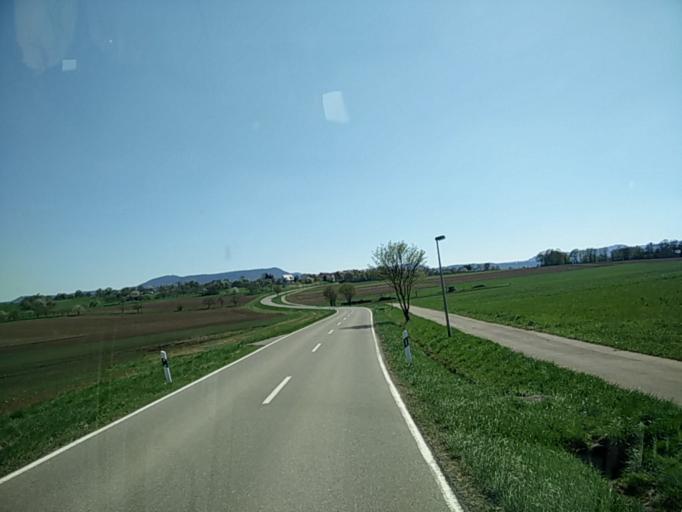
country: DE
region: Baden-Wuerttemberg
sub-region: Tuebingen Region
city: Gomaringen
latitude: 48.4700
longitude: 9.0881
